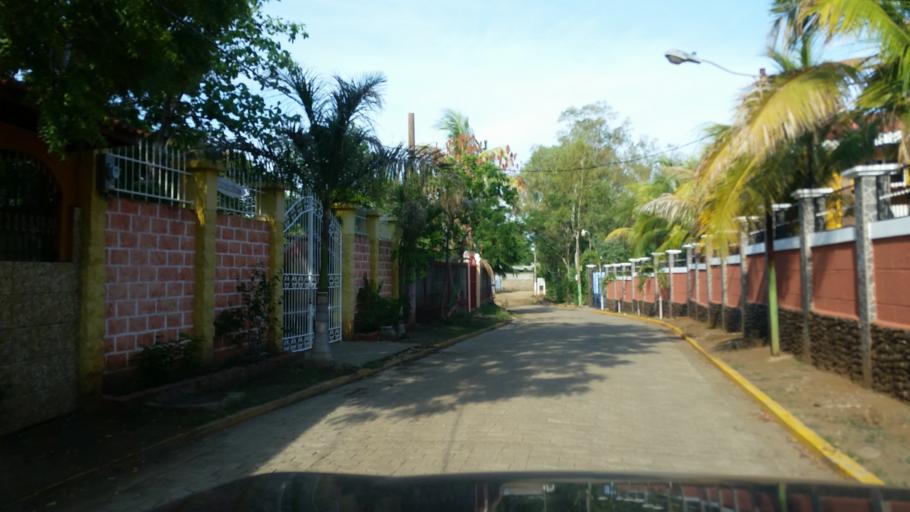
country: NI
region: Managua
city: Masachapa
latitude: 11.7762
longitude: -86.5140
